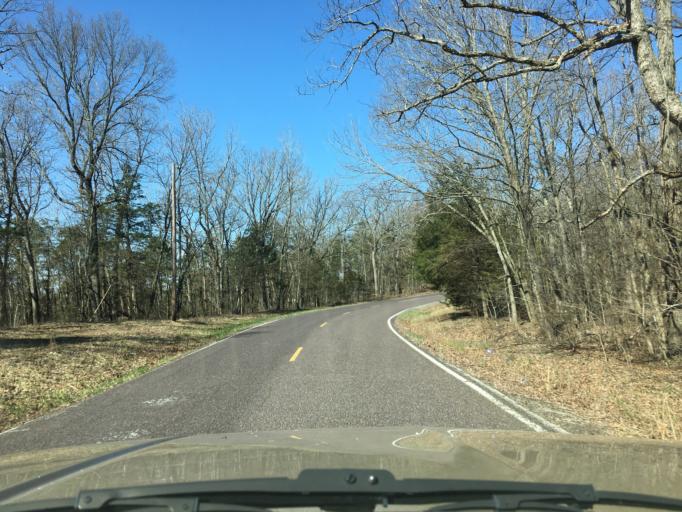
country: US
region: Missouri
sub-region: Franklin County
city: Gerald
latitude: 38.5176
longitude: -91.3250
